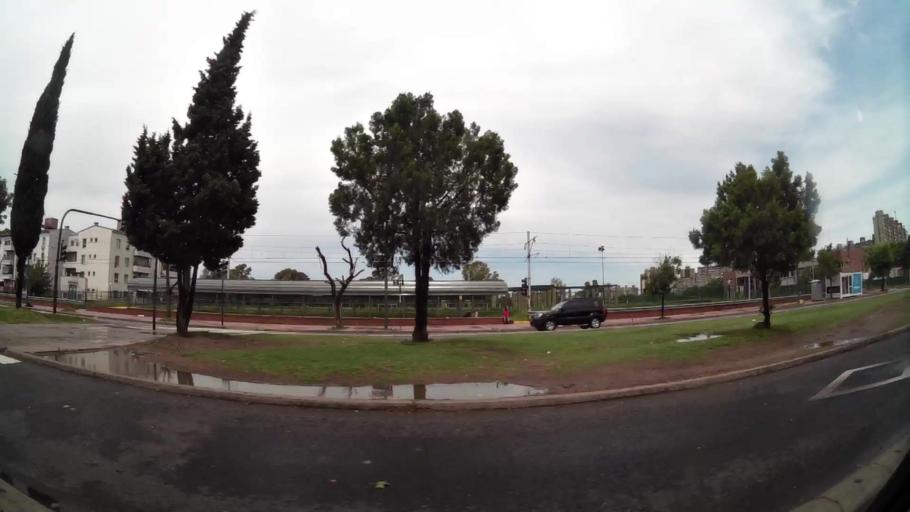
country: AR
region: Buenos Aires F.D.
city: Villa Lugano
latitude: -34.6781
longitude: -58.4650
